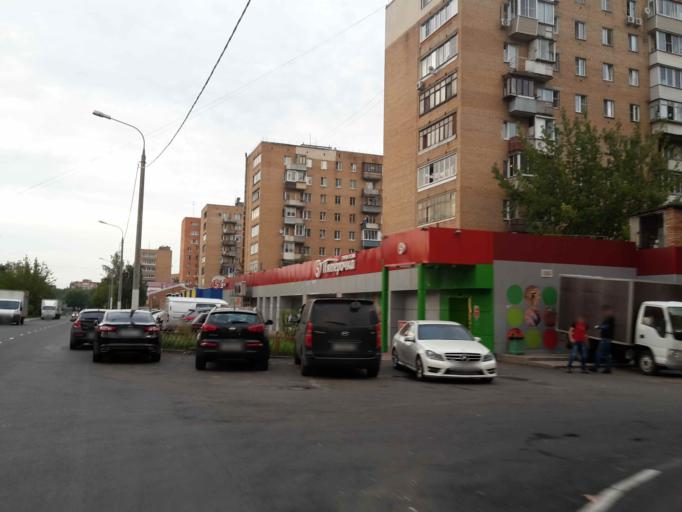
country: RU
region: Moskovskaya
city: Dolgoprudnyy
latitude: 55.9388
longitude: 37.5035
